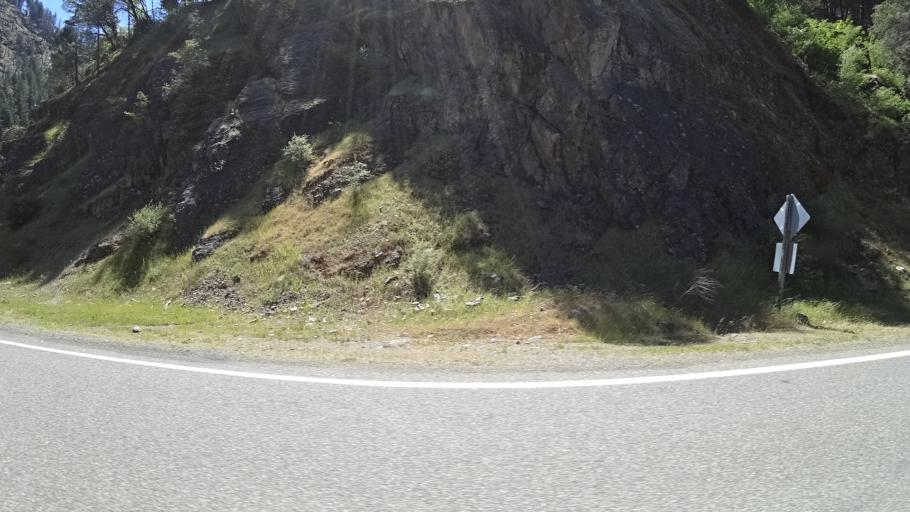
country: US
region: California
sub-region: Trinity County
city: Weaverville
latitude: 40.7656
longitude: -123.1362
